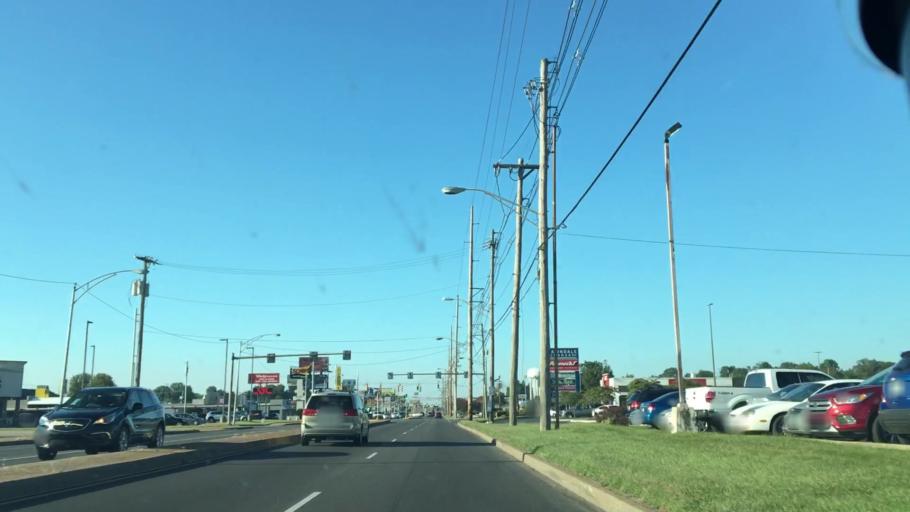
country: US
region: Indiana
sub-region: Vanderburgh County
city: Evansville
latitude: 37.9627
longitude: -87.4926
